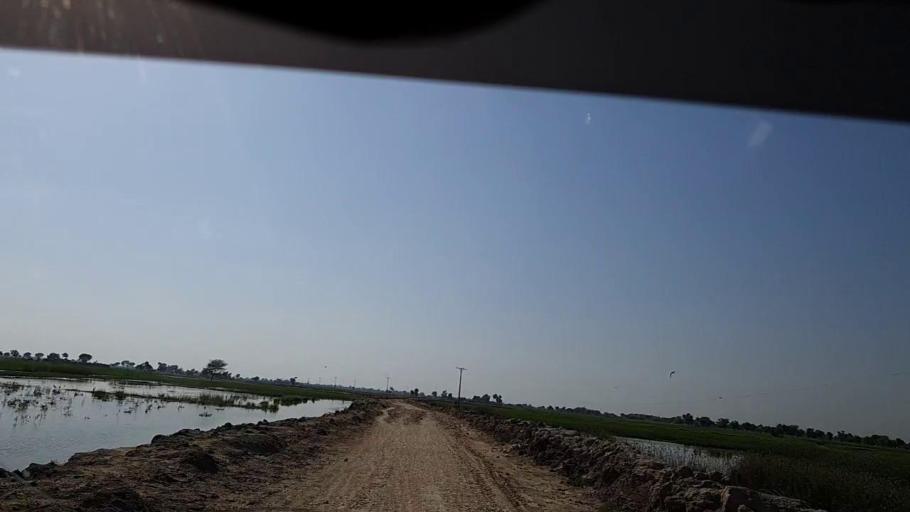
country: PK
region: Sindh
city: Tangwani
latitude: 28.3611
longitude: 69.0240
